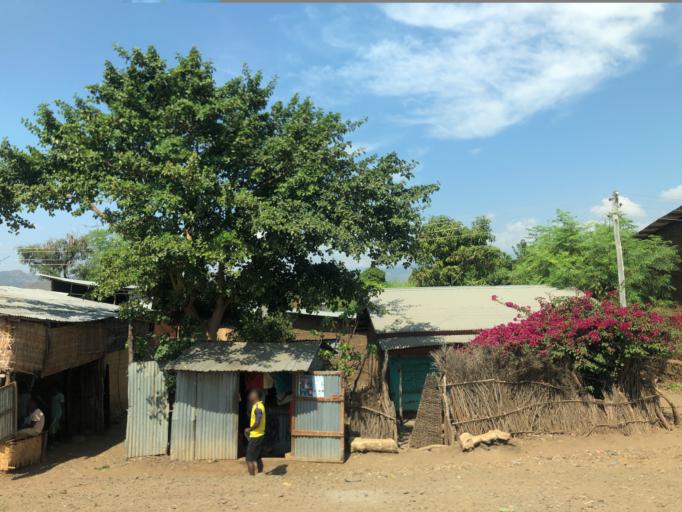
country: ET
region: Southern Nations, Nationalities, and People's Region
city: Arba Minch'
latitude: 5.8447
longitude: 37.4646
